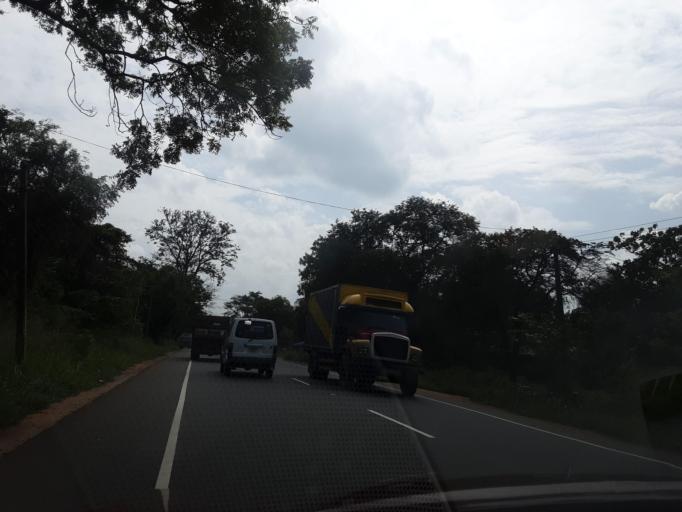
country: LK
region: North Central
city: Anuradhapura
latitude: 8.4838
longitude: 80.5097
